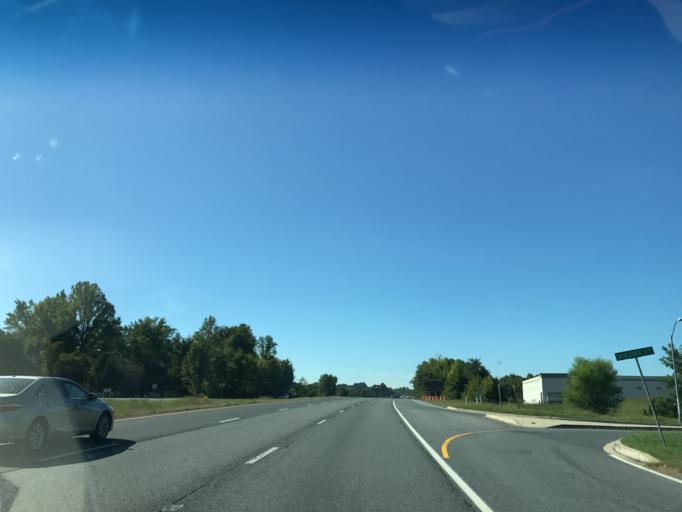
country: US
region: Maryland
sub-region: Prince George's County
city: Marlboro Meadows
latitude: 38.8717
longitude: -76.7216
